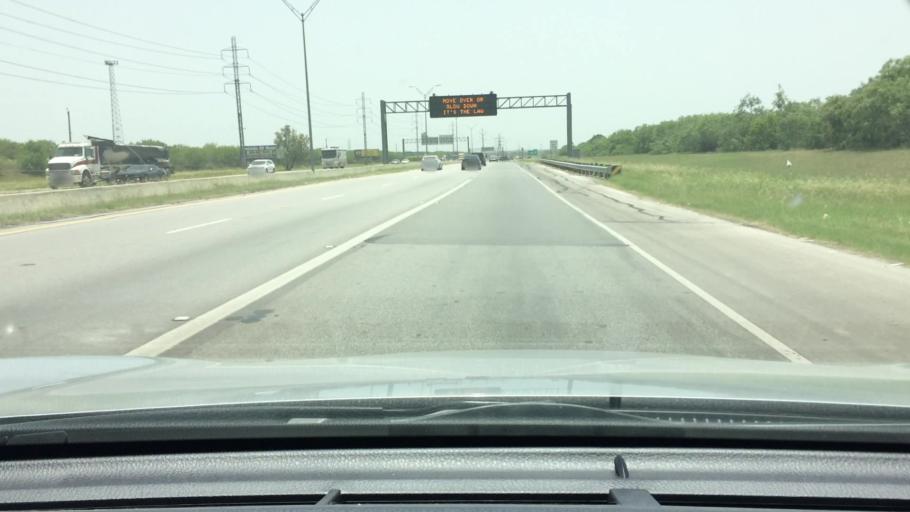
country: US
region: Texas
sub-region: Bexar County
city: China Grove
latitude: 29.3480
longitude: -98.4253
